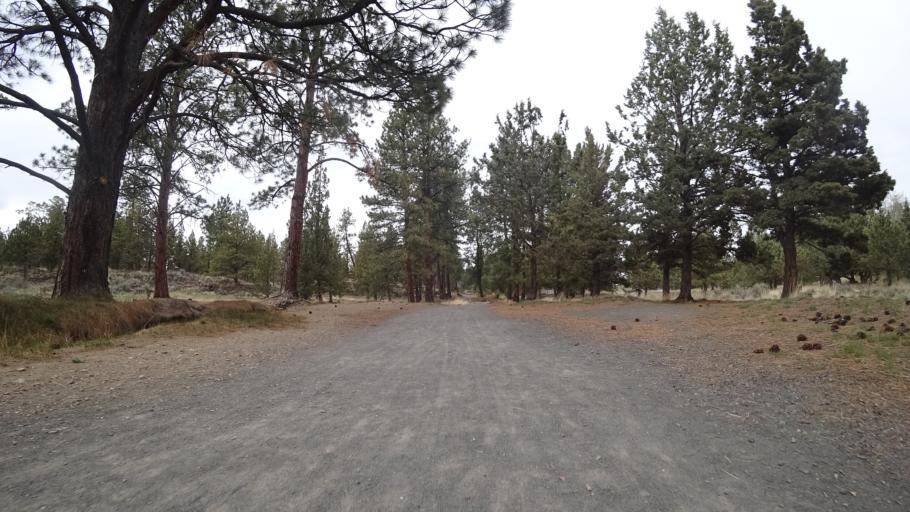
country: US
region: Oregon
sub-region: Deschutes County
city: Bend
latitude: 44.0433
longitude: -121.2781
